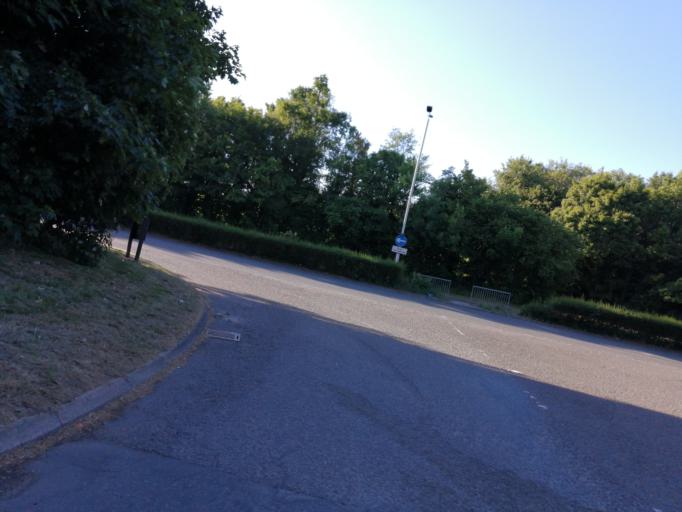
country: GB
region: England
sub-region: Peterborough
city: Marholm
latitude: 52.6040
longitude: -0.2836
